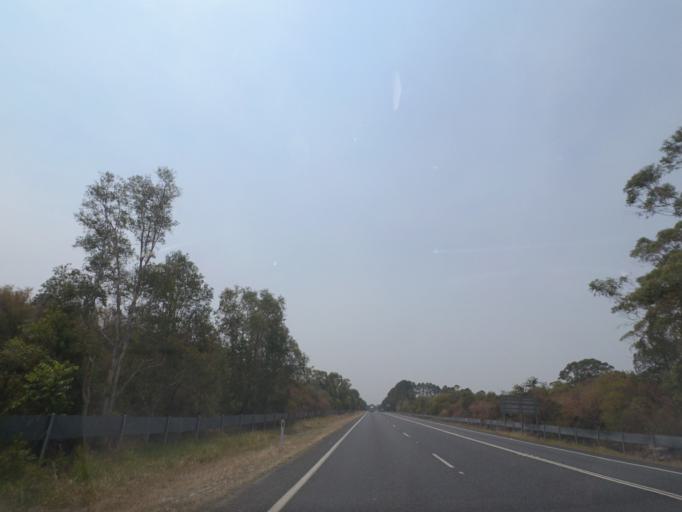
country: AU
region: New South Wales
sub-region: Ballina
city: Ballina
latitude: -28.9438
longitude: 153.4683
